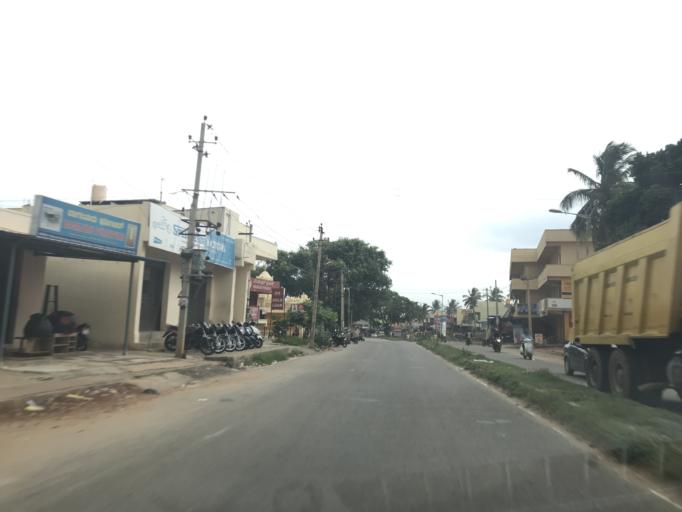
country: IN
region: Karnataka
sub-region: Bangalore Urban
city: Yelahanka
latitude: 13.1325
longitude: 77.6646
